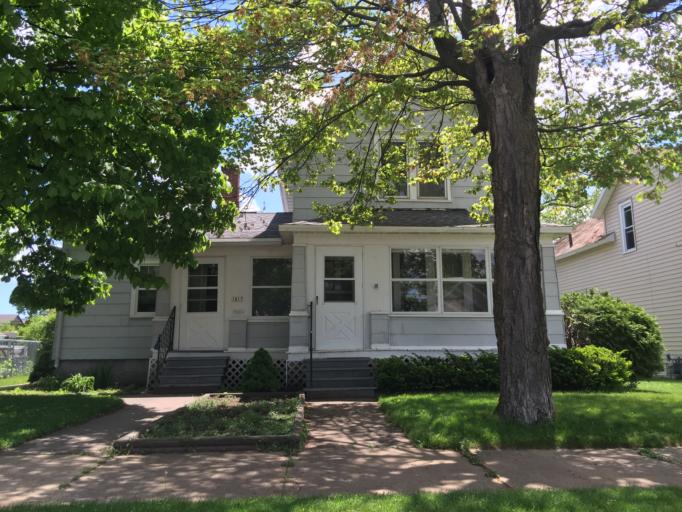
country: US
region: Wisconsin
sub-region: Marinette County
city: Marinette
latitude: 45.1107
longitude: -87.6261
